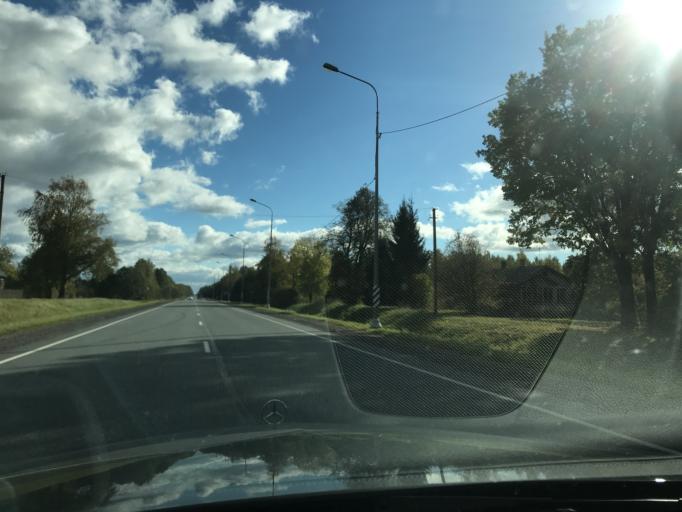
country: RU
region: Pskov
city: Ostrov
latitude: 57.2603
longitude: 28.4158
